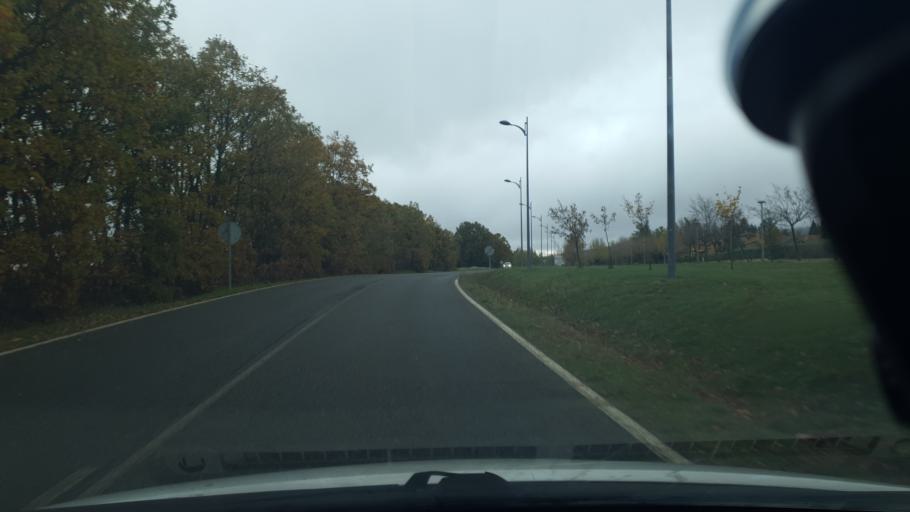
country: ES
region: Castille and Leon
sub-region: Provincia de Segovia
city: Riaza
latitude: 41.2734
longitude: -3.4920
